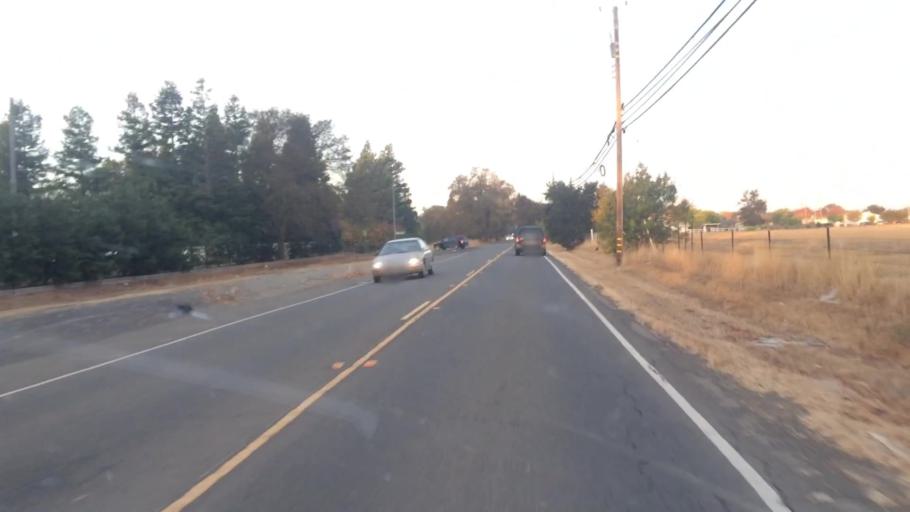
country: US
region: California
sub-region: Sacramento County
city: Vineyard
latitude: 38.4382
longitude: -121.3178
